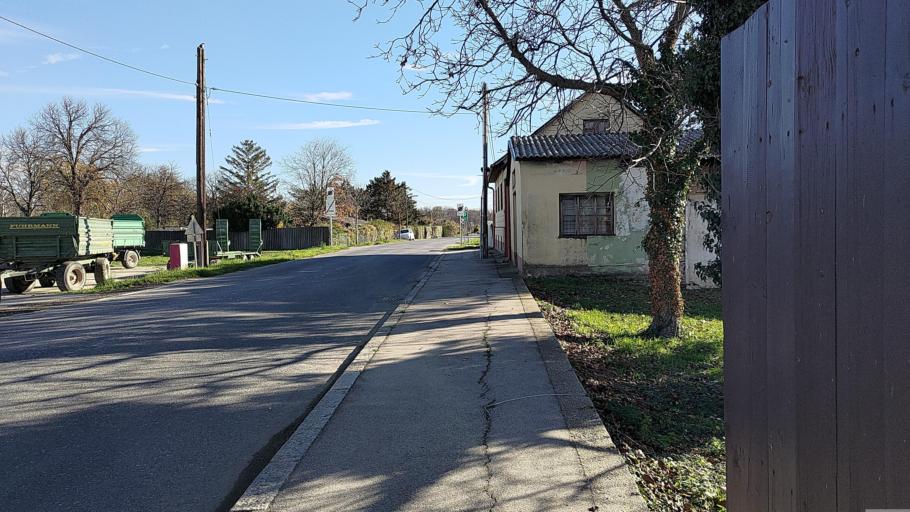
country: AT
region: Lower Austria
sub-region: Politischer Bezirk Wien-Umgebung
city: Schwechat
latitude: 48.1585
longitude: 16.4905
